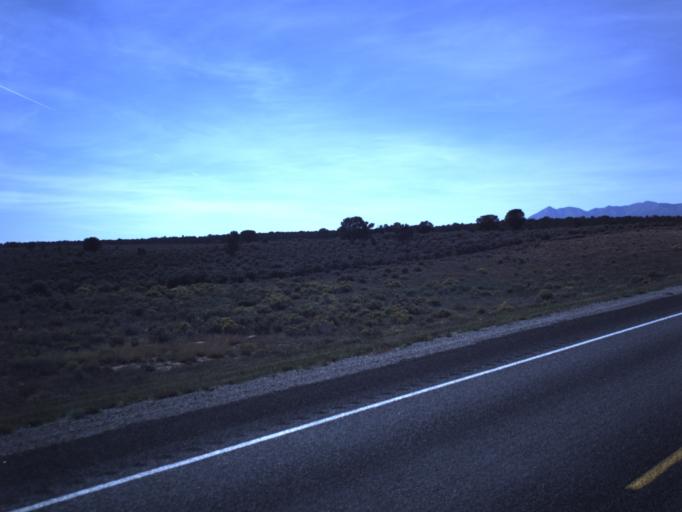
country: US
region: Colorado
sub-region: Dolores County
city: Dove Creek
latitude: 37.8343
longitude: -109.1039
